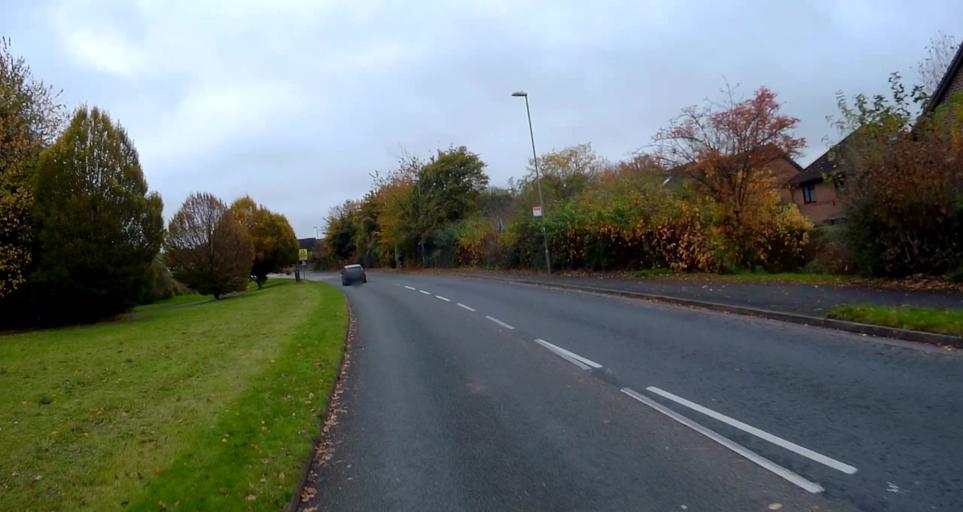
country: GB
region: England
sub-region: Hampshire
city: Basingstoke
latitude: 51.2334
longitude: -1.1319
